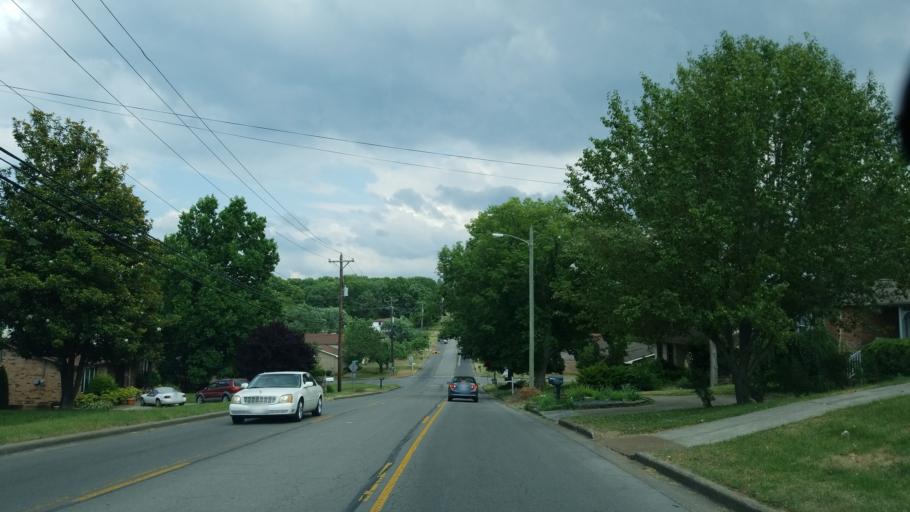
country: US
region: Tennessee
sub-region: Rutherford County
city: La Vergne
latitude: 36.0736
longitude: -86.6204
